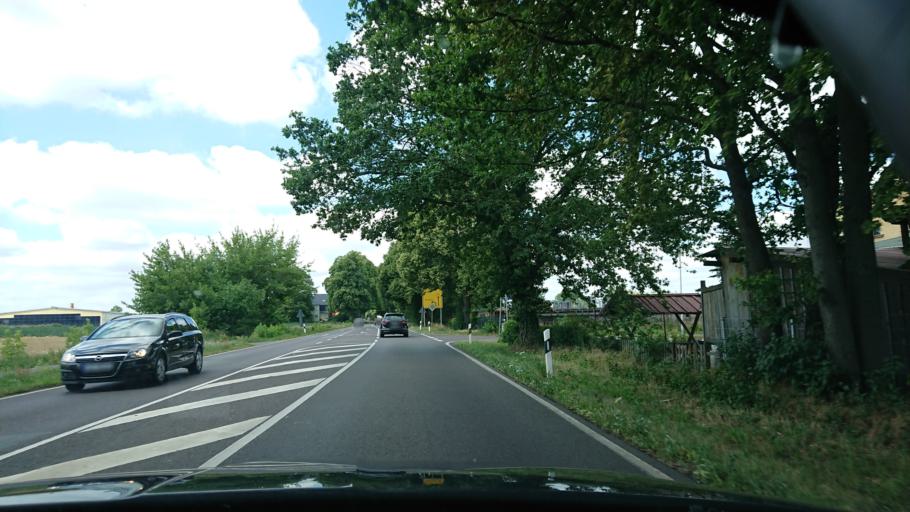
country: DE
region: Brandenburg
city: Perleberg
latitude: 53.0687
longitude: 11.8810
